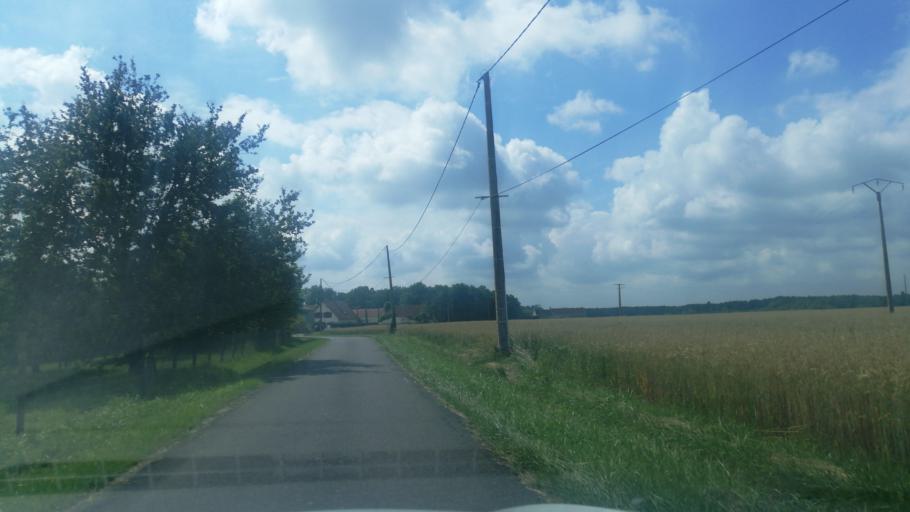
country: FR
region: Centre
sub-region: Departement du Loir-et-Cher
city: Saint-Romain-sur-Cher
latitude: 47.3583
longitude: 1.3922
